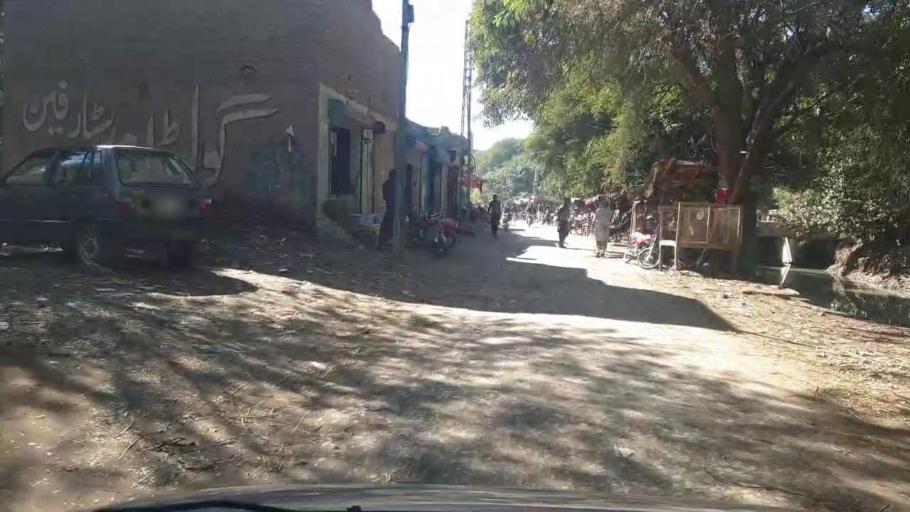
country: PK
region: Sindh
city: Bozdar
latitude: 27.0672
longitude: 68.6172
